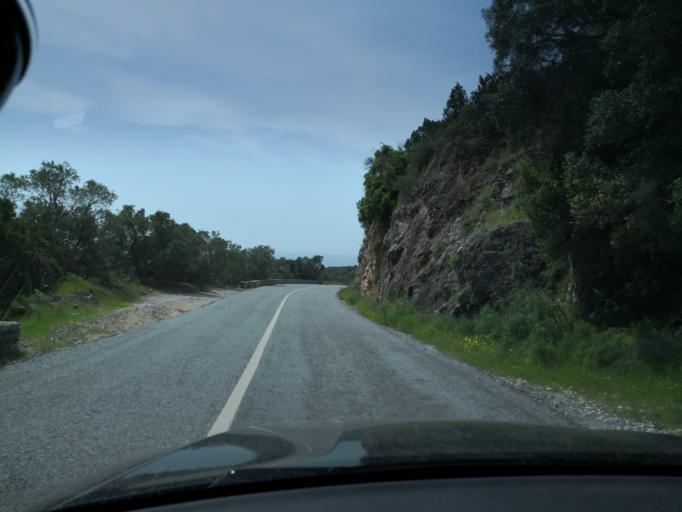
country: PT
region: Setubal
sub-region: Palmela
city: Quinta do Anjo
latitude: 38.4772
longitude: -8.9867
